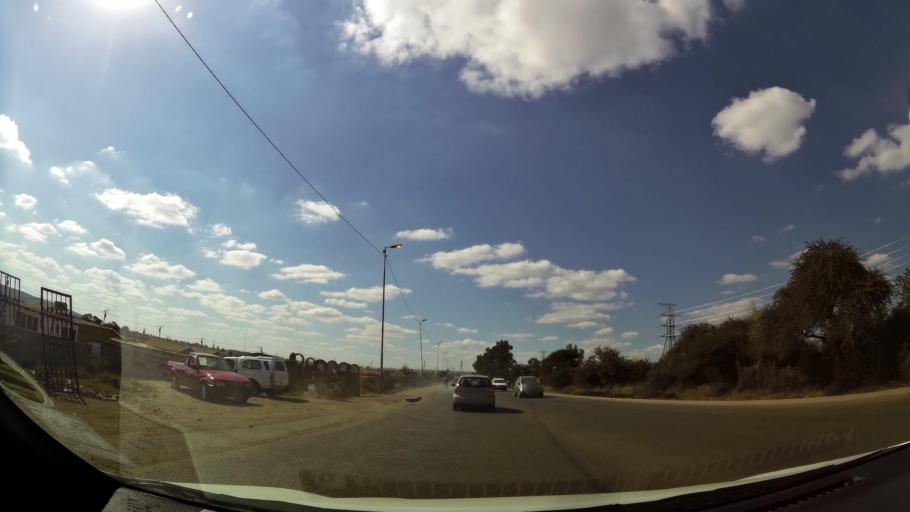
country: ZA
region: Gauteng
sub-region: City of Tshwane Metropolitan Municipality
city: Cullinan
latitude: -25.7363
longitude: 28.3939
